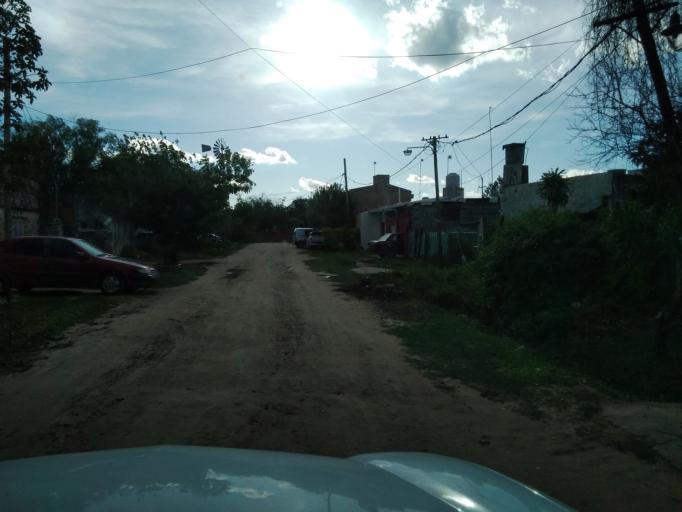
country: AR
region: Corrientes
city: Corrientes
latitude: -27.4914
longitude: -58.8474
